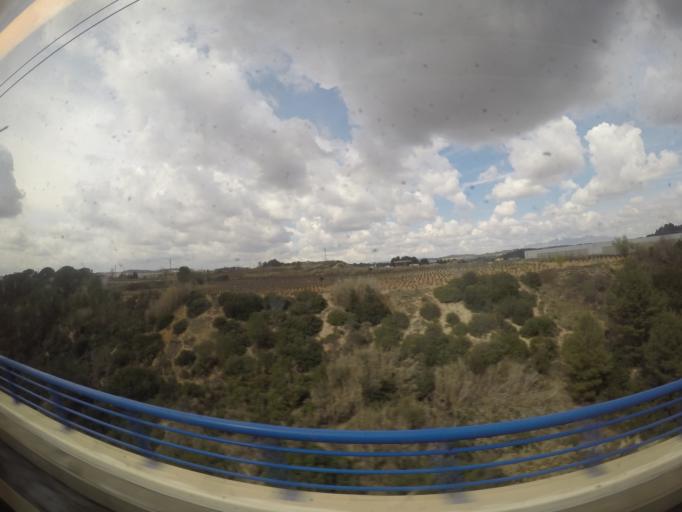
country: ES
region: Catalonia
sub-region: Provincia de Barcelona
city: Sant Sadurni d'Anoia
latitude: 41.4221
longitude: 1.8014
